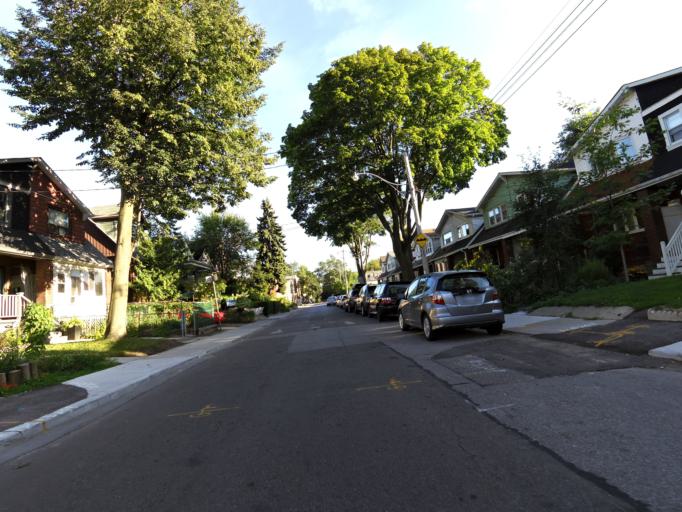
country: CA
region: Ontario
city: Toronto
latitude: 43.6729
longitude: -79.3244
